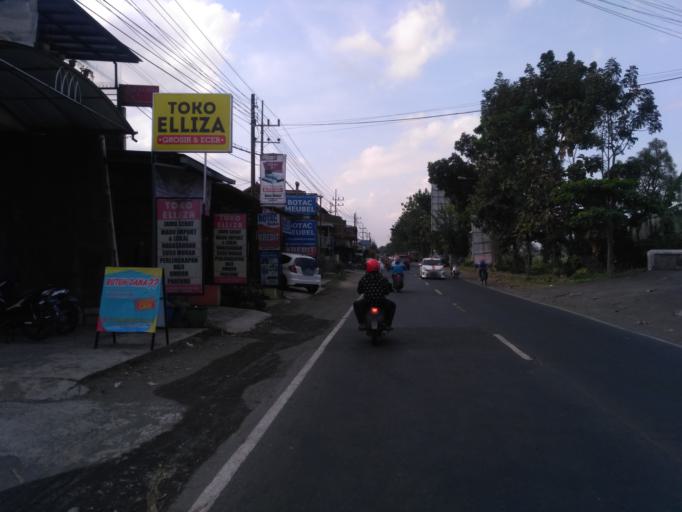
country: ID
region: East Java
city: Pakisaji
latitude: -8.0590
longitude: 112.6015
